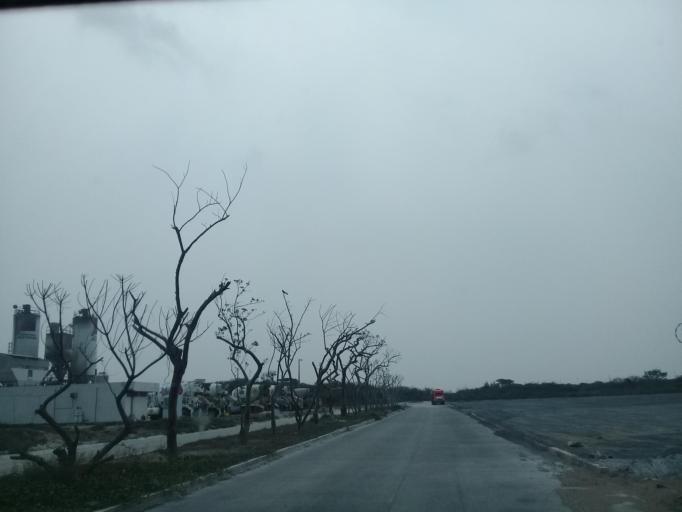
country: MX
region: Veracruz
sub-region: Veracruz
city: Colonia el Renacimiento
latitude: 19.2290
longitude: -96.1973
